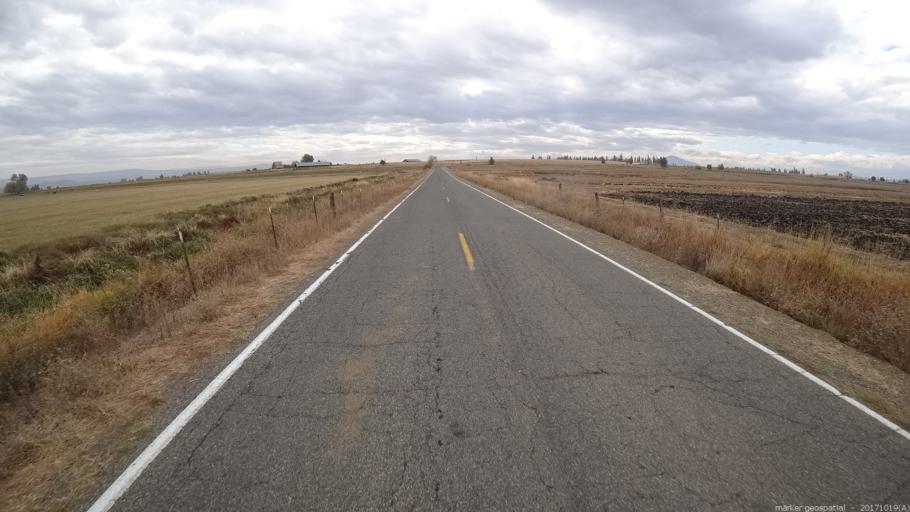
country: US
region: California
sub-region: Shasta County
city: Burney
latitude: 41.0461
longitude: -121.3903
